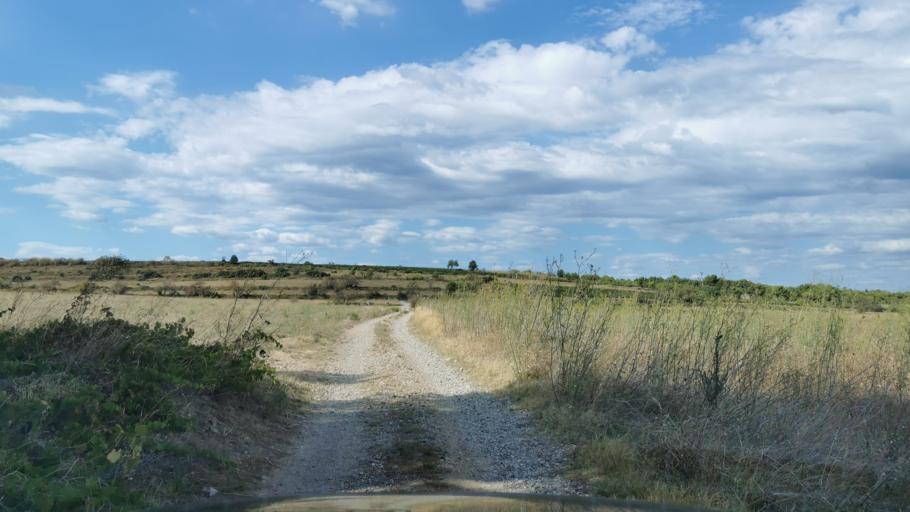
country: FR
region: Languedoc-Roussillon
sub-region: Departement de l'Aude
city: Ginestas
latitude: 43.2873
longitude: 2.8626
